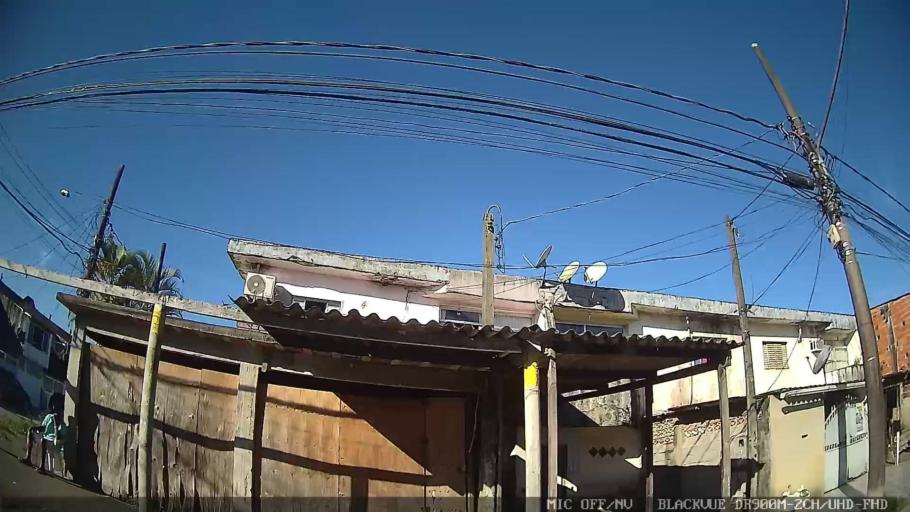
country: BR
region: Sao Paulo
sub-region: Guaruja
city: Guaruja
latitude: -23.9558
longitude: -46.2773
